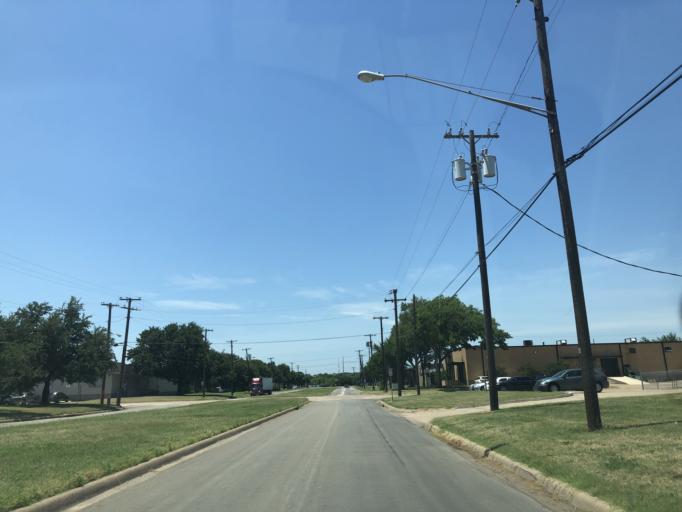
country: US
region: Texas
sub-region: Dallas County
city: Irving
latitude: 32.8162
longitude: -96.8933
